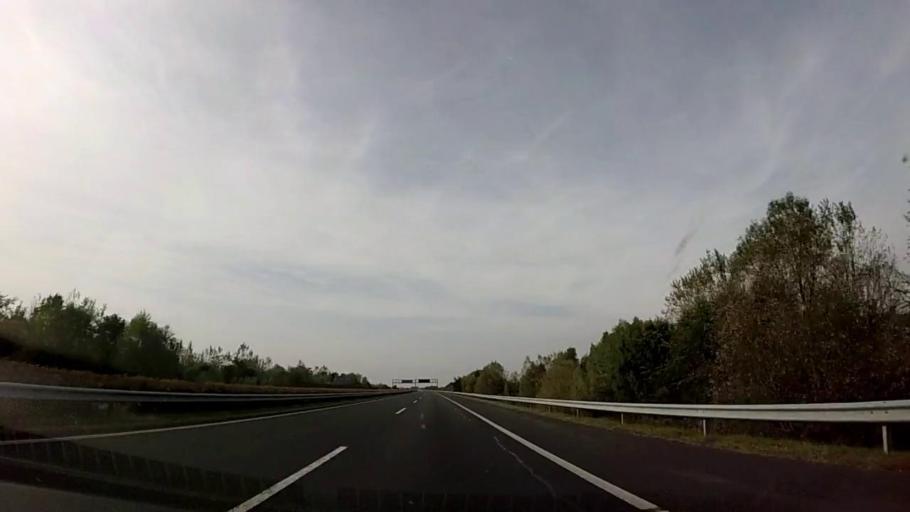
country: HU
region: Somogy
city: Balatonboglar
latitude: 46.7508
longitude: 17.6226
